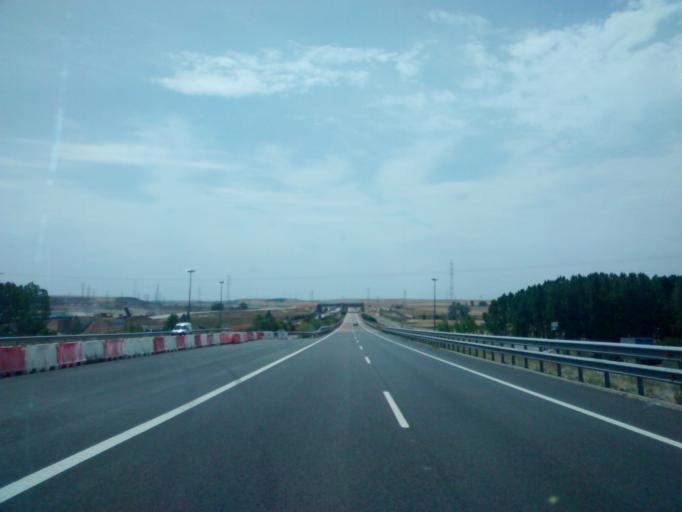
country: ES
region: Castille and Leon
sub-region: Provincia de Burgos
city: San Mames de Burgos
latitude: 42.3508
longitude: -3.7956
